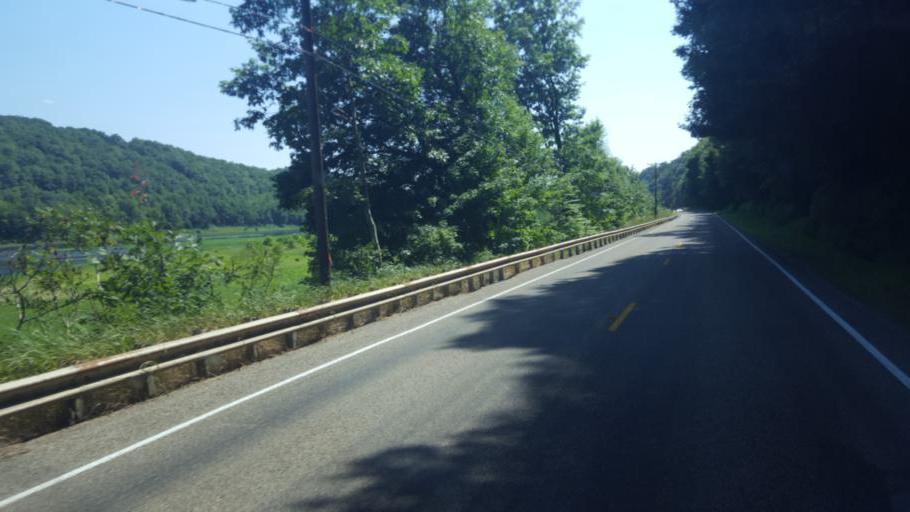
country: US
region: Pennsylvania
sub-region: Butler County
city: Chicora
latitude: 41.1105
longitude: -79.6809
